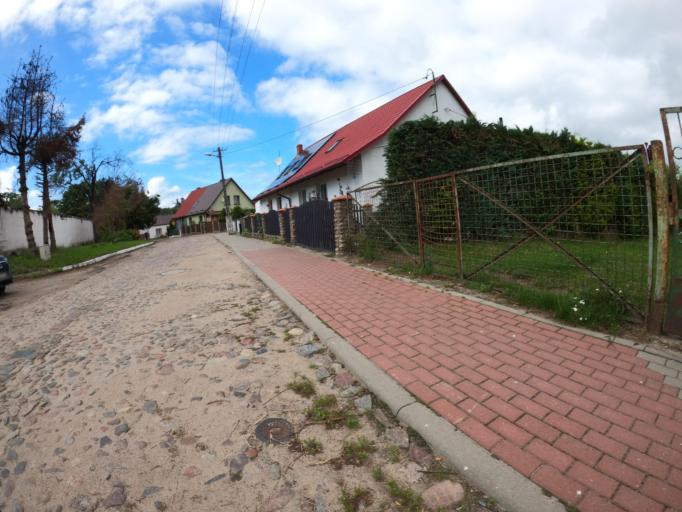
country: PL
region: West Pomeranian Voivodeship
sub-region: Powiat bialogardzki
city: Tychowo
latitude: 54.0026
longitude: 16.3740
